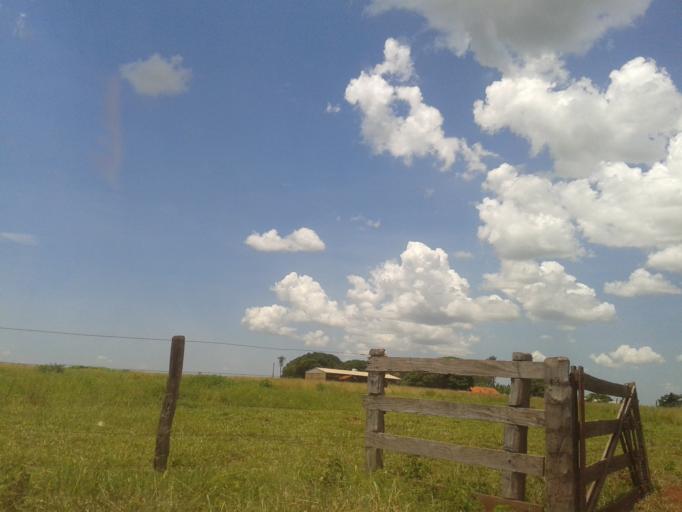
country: BR
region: Minas Gerais
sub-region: Santa Vitoria
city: Santa Vitoria
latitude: -19.1635
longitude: -50.4224
